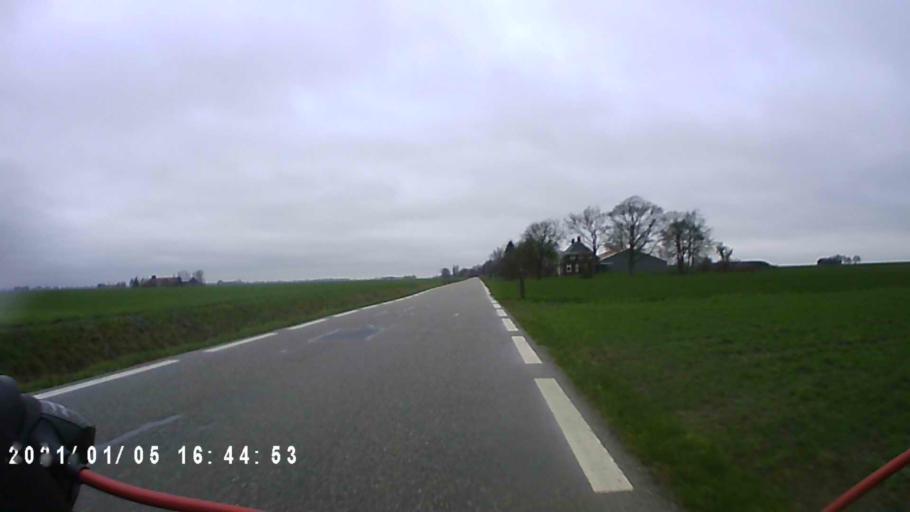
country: NL
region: Groningen
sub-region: Gemeente  Oldambt
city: Winschoten
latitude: 53.2189
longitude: 7.0521
